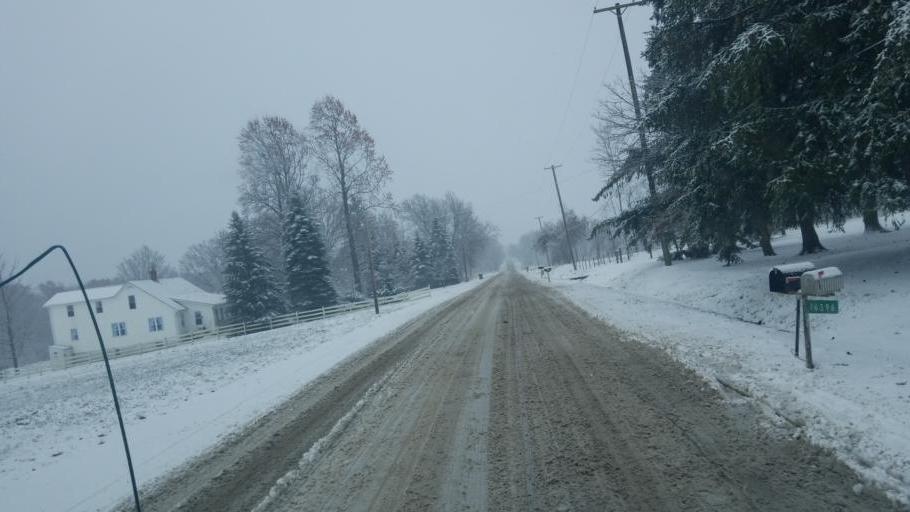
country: US
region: Ohio
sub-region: Geauga County
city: Middlefield
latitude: 41.4233
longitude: -81.0803
